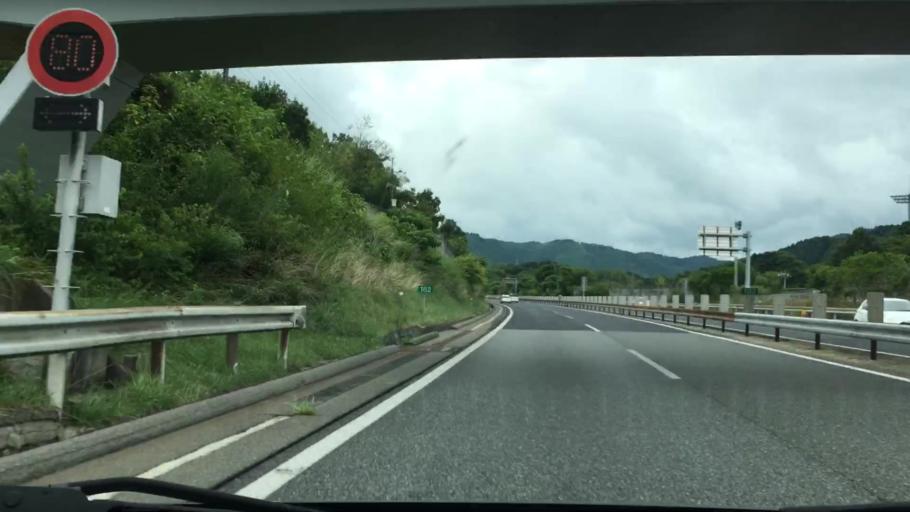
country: JP
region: Okayama
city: Tsuyama
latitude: 35.0252
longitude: 133.7444
